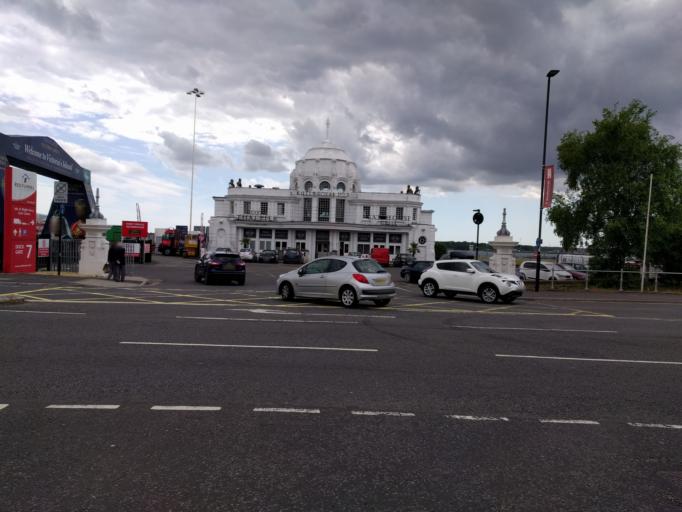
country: GB
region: England
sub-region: Southampton
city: Southampton
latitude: 50.8974
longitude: -1.4064
